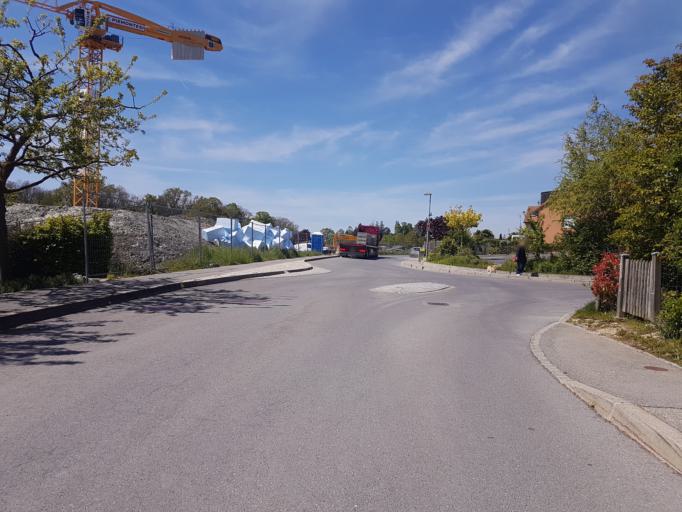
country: CH
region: Neuchatel
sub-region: Neuchatel District
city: Saint-Blaise
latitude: 47.0077
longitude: 7.0158
